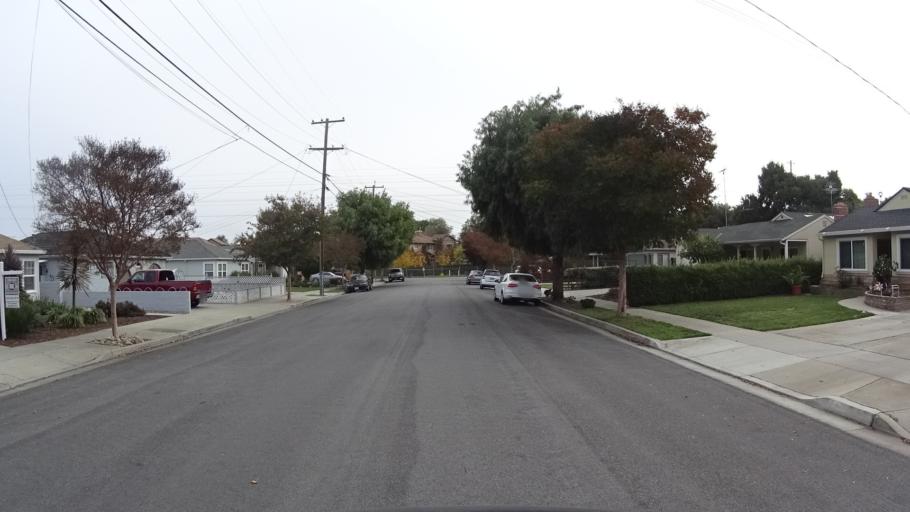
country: US
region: California
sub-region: Santa Clara County
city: Sunnyvale
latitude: 37.3712
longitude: -122.0194
